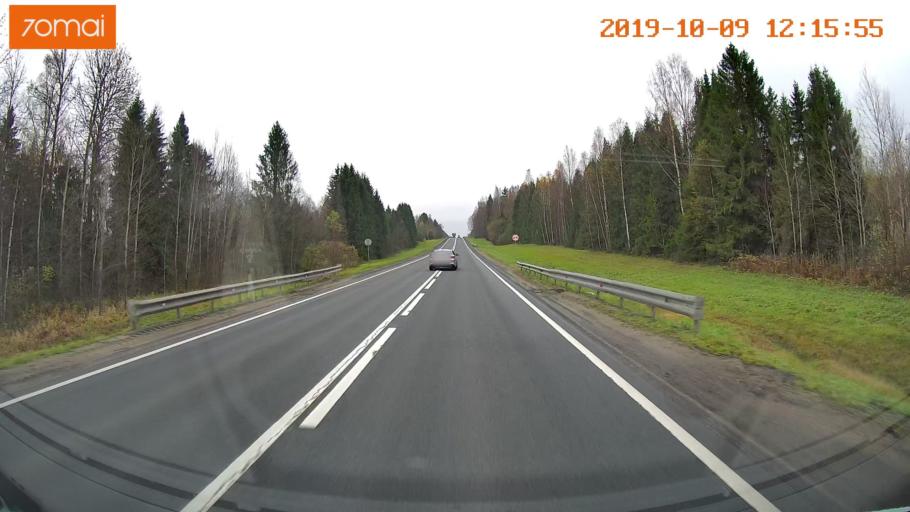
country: RU
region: Jaroslavl
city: Prechistoye
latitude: 58.4761
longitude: 40.3221
